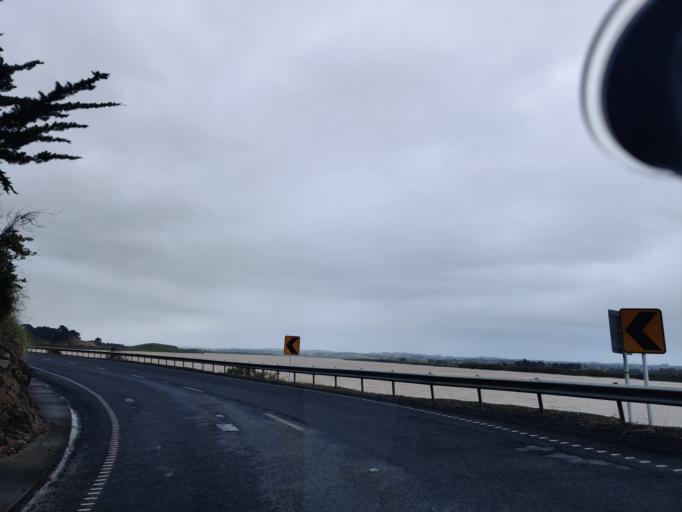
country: NZ
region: Northland
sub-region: Kaipara District
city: Dargaville
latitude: -36.0593
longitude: 173.9668
